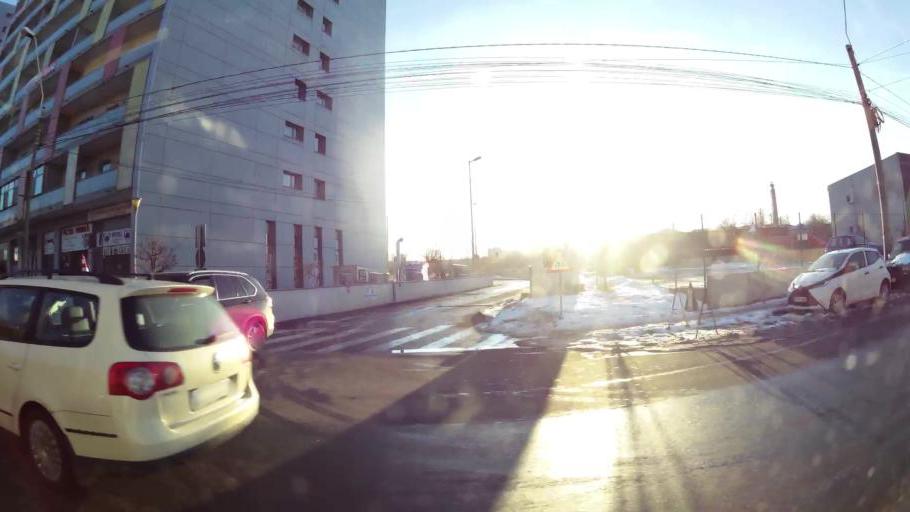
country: RO
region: Ilfov
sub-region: Comuna Fundeni-Dobroesti
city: Fundeni
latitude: 44.4525
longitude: 26.1442
